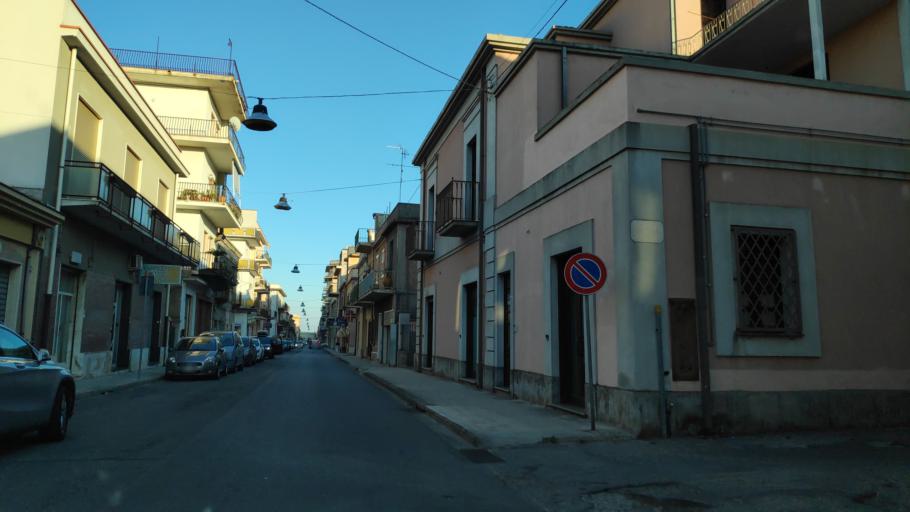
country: IT
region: Calabria
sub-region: Provincia di Reggio Calabria
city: Locri
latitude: 38.2355
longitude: 16.2609
